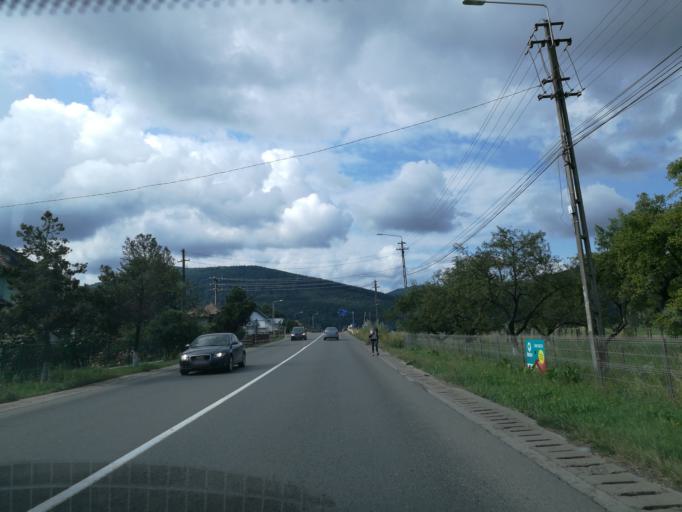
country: RO
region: Suceava
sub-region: Comuna Paltinoasa
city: Paltinoasa
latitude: 47.5477
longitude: 25.9502
